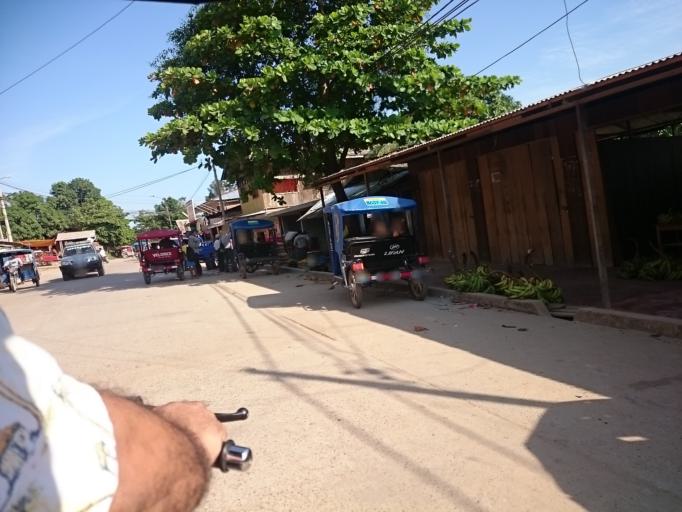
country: PE
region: Ucayali
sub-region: Provincia de Coronel Portillo
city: Puerto Callao
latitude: -8.3523
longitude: -74.5765
